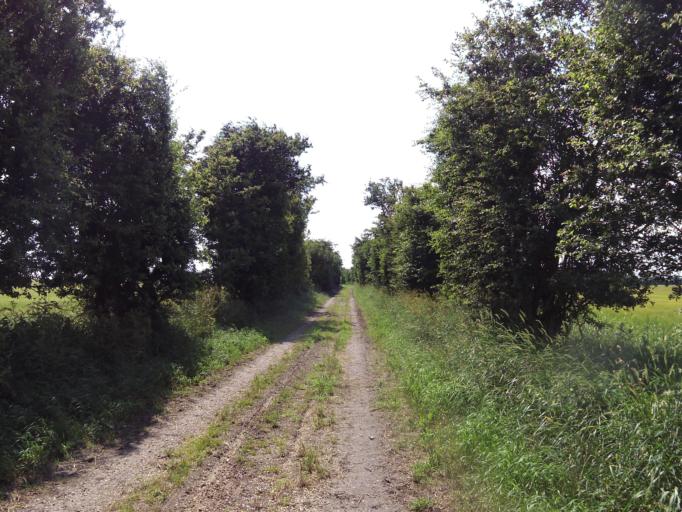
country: DK
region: South Denmark
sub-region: Aabenraa Kommune
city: Rodekro
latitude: 55.1504
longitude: 9.2468
